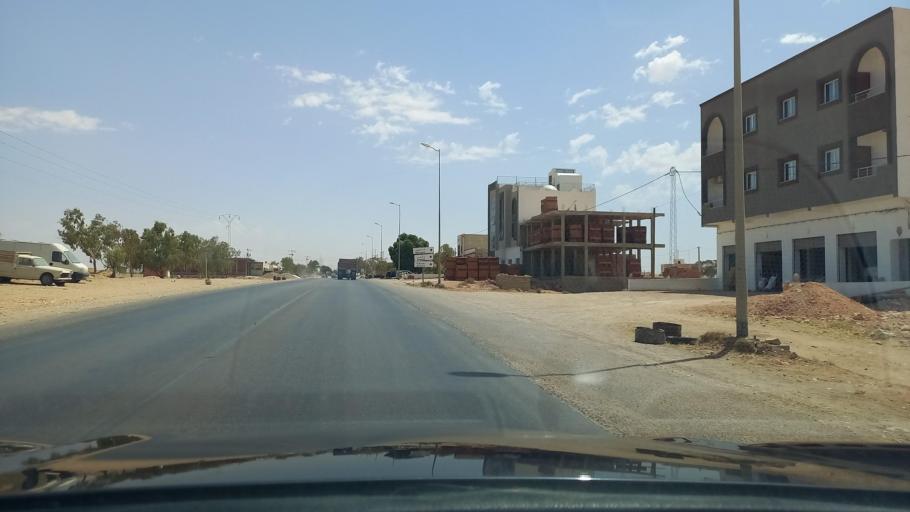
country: TN
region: Madanin
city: Medenine
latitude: 33.3746
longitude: 10.4456
